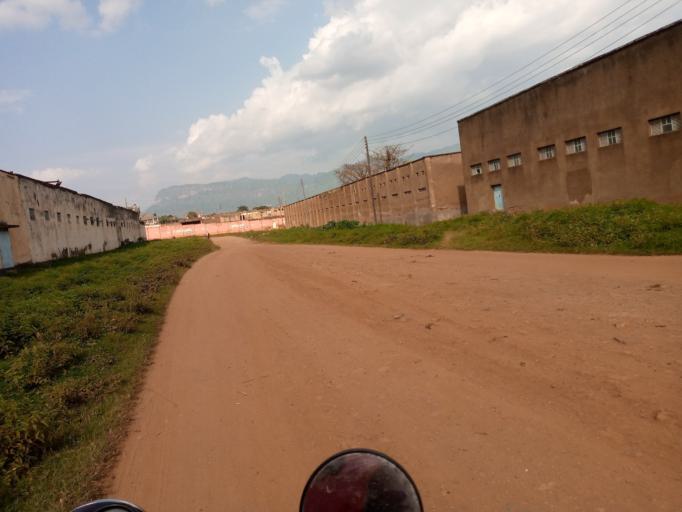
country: UG
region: Eastern Region
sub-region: Mbale District
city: Mbale
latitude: 1.0784
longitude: 34.1637
